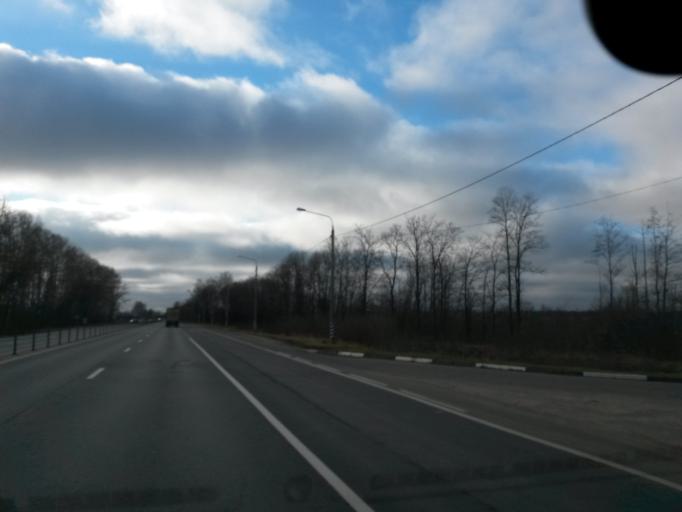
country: RU
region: Jaroslavl
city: Semibratovo
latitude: 57.3287
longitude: 39.5708
